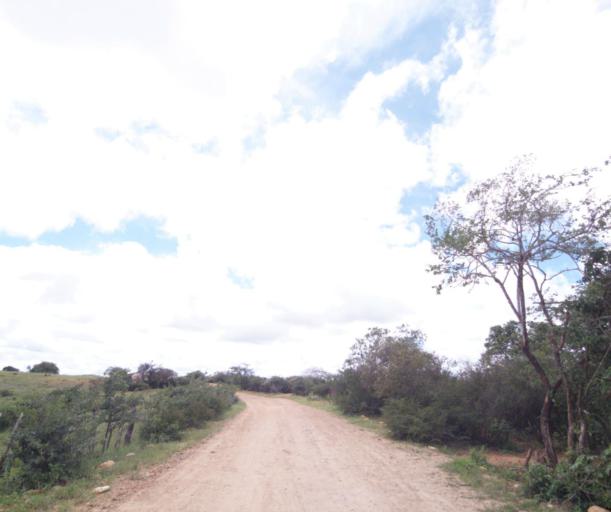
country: BR
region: Bahia
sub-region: Tanhacu
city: Tanhacu
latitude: -14.1675
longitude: -41.1431
